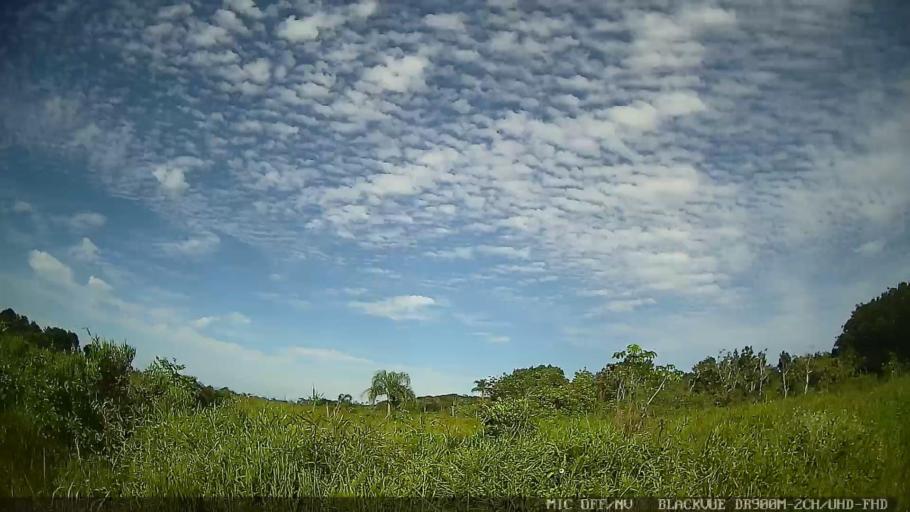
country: BR
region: Sao Paulo
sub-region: Iguape
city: Iguape
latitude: -24.7641
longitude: -47.5878
